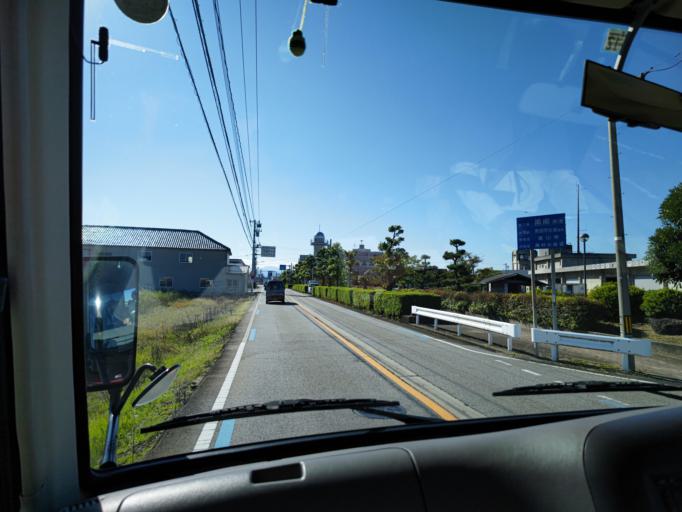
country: JP
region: Toyama
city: Nyuzen
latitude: 36.8934
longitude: 137.4195
